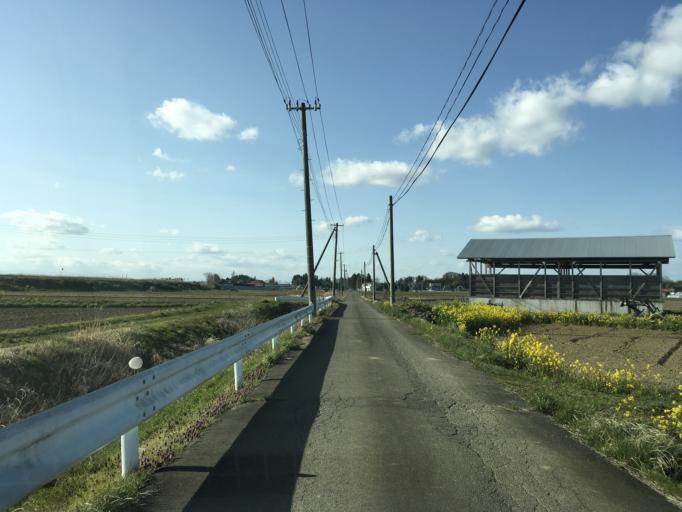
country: JP
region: Miyagi
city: Wakuya
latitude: 38.6626
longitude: 141.2169
